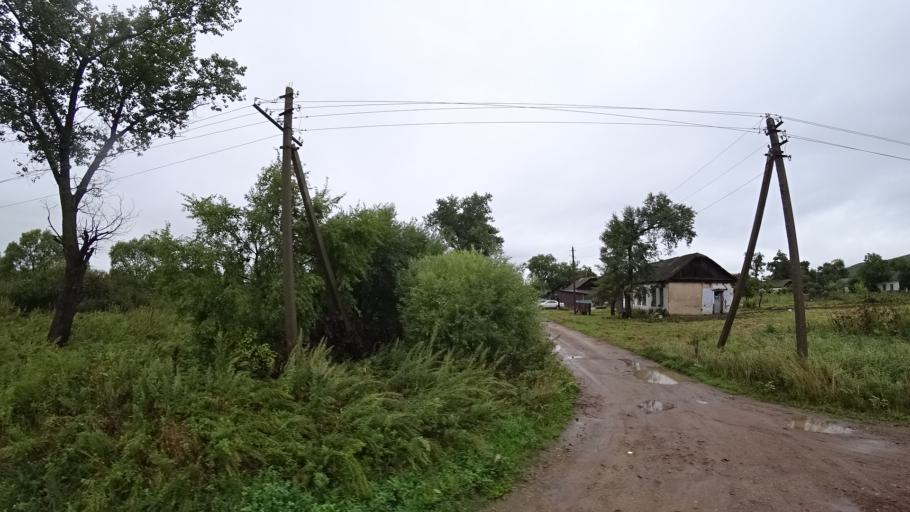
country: RU
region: Primorskiy
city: Monastyrishche
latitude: 44.2335
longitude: 132.4637
